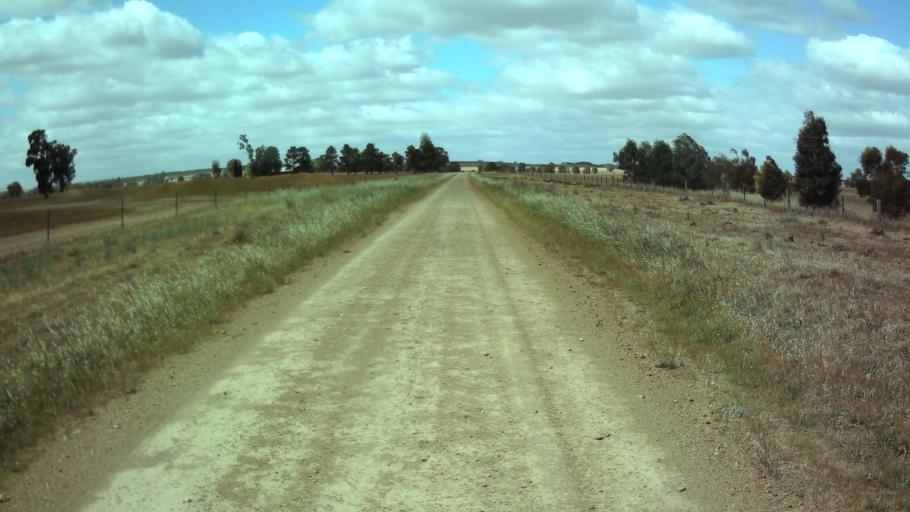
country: AU
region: New South Wales
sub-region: Weddin
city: Grenfell
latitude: -34.0562
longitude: 148.3311
